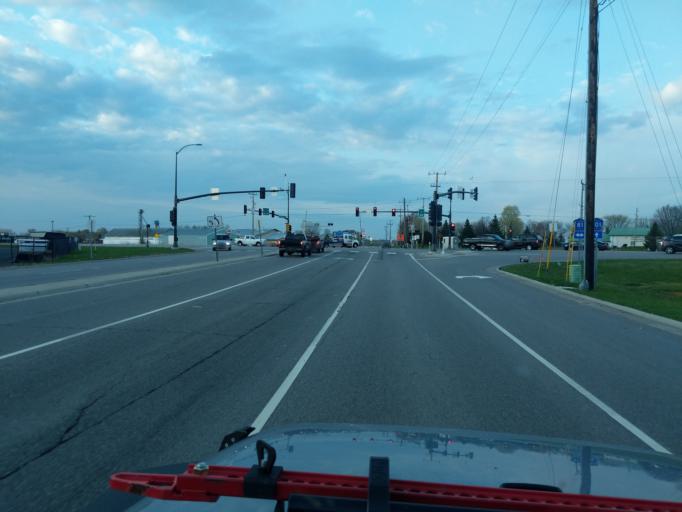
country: US
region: Minnesota
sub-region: Hennepin County
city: Rogers
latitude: 45.1704
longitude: -93.5217
